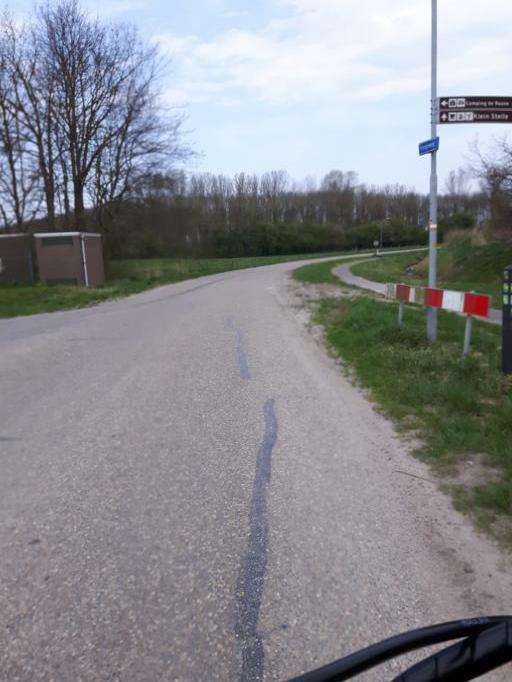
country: NL
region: Zeeland
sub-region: Gemeente Reimerswaal
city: Yerseke
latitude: 51.5202
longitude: 3.9830
